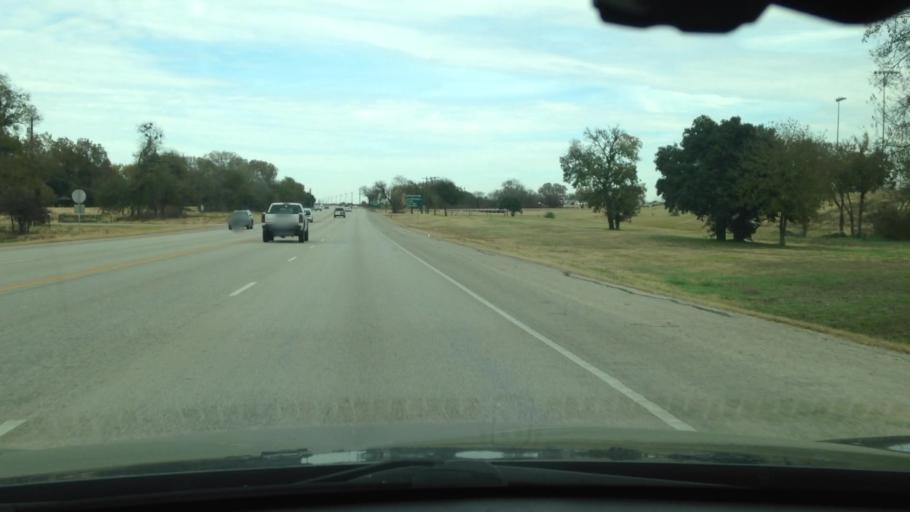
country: US
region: Texas
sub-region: Hays County
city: San Marcos
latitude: 29.8834
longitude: -97.8943
